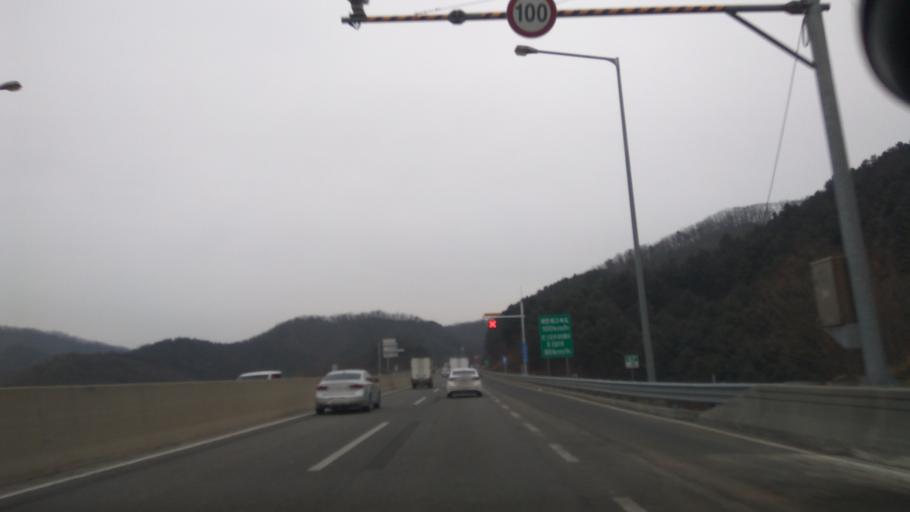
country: KR
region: Gangwon-do
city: Sindong
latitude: 37.7368
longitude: 127.6301
